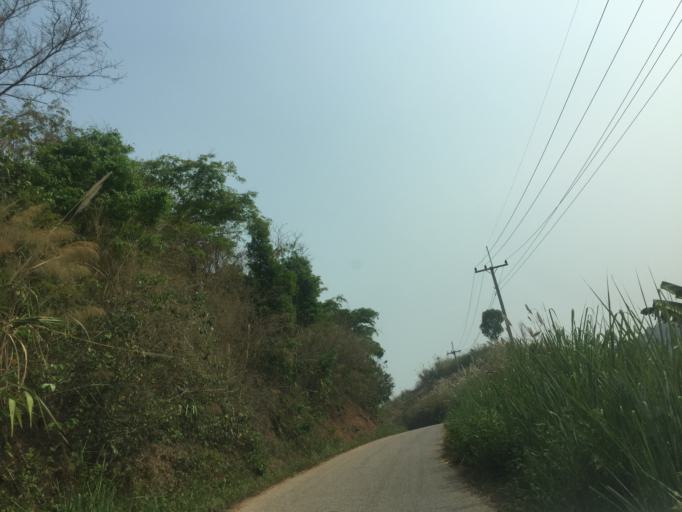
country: LA
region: Xiagnabouli
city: Sainyabuli
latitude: 19.3036
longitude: 101.4807
